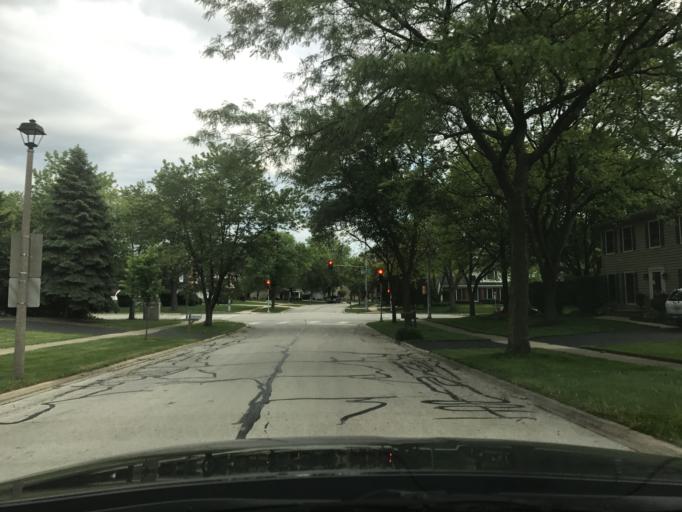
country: US
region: Illinois
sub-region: DuPage County
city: Naperville
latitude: 41.7583
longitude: -88.1139
